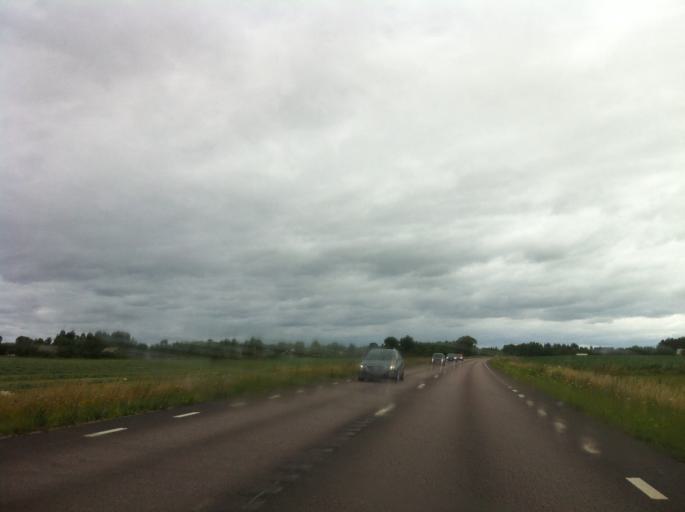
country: SE
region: Kalmar
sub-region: Borgholms Kommun
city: Borgholm
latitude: 57.0936
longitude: 16.9264
